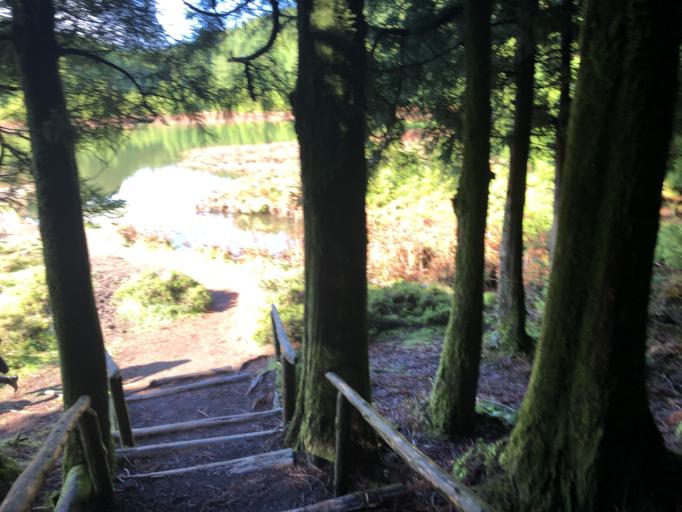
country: PT
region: Azores
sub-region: Ponta Delgada
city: Arrifes
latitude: 37.8366
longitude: -25.7587
